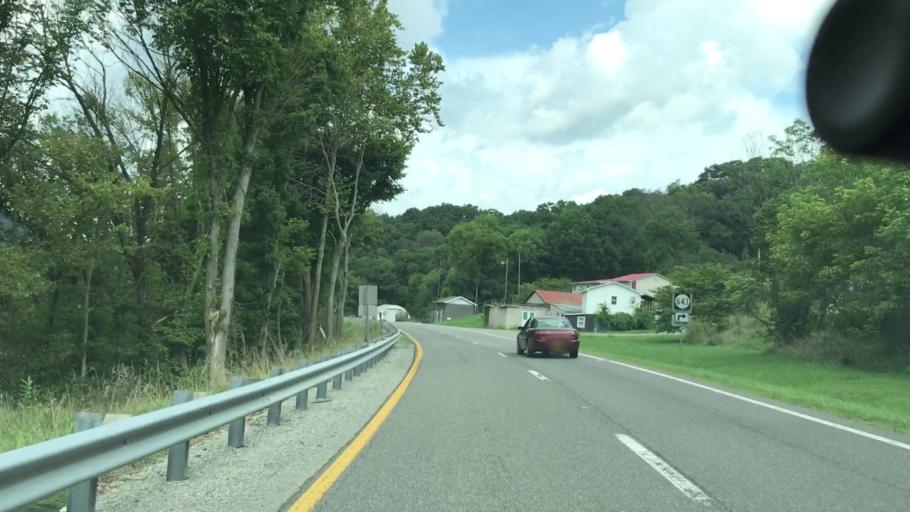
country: US
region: Virginia
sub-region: Giles County
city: Narrows
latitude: 37.3609
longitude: -80.8134
